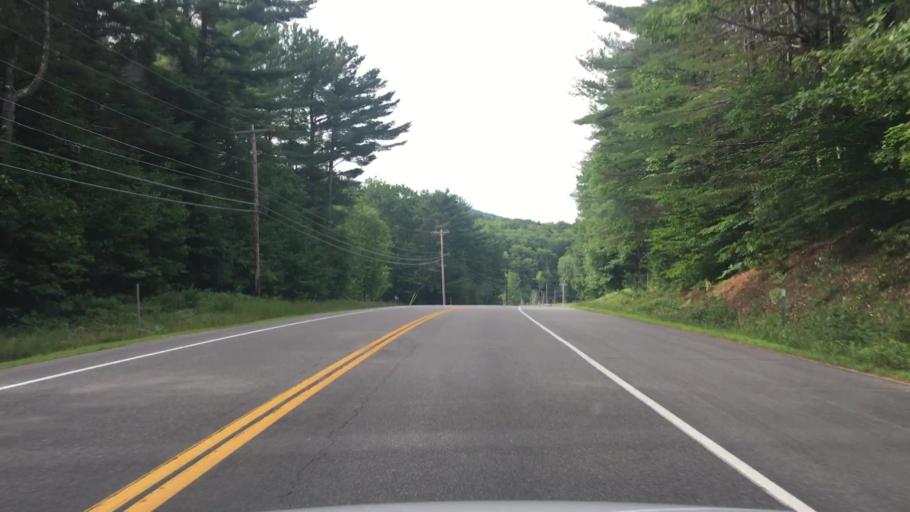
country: US
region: New Hampshire
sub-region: Carroll County
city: Sandwich
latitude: 43.8105
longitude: -71.3537
